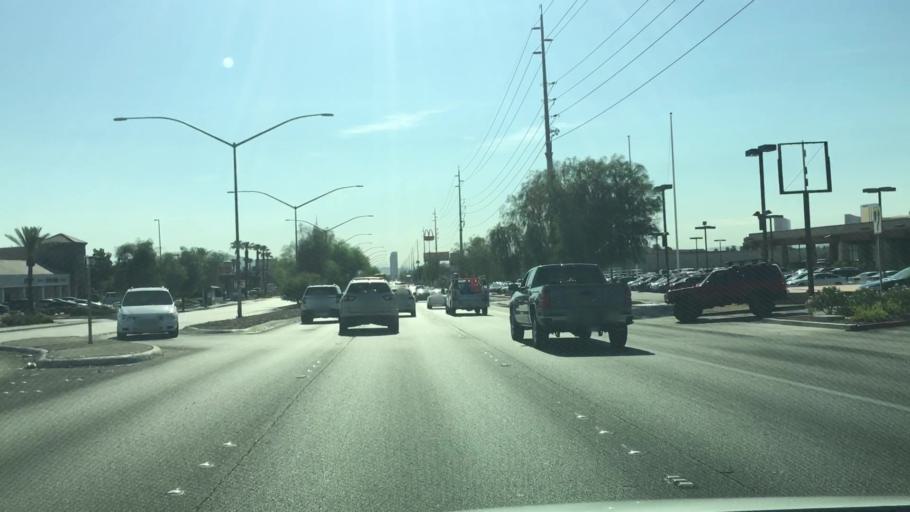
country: US
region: Nevada
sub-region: Clark County
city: Spring Valley
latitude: 36.1444
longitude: -115.2062
